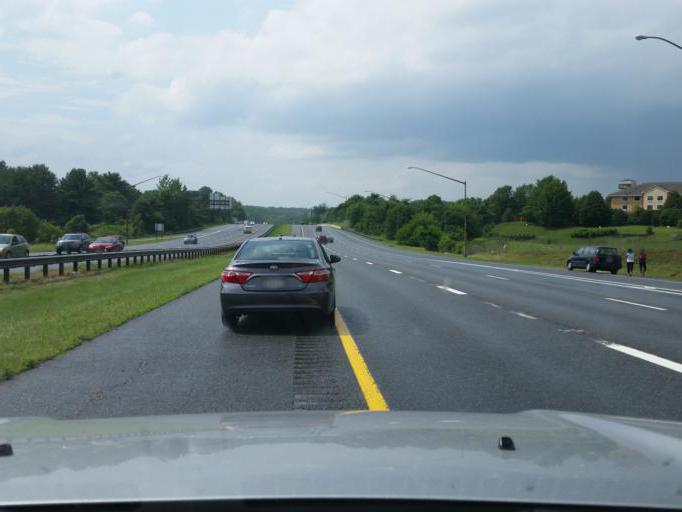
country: US
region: Maryland
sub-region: Montgomery County
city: Germantown
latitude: 39.1999
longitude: -77.2654
